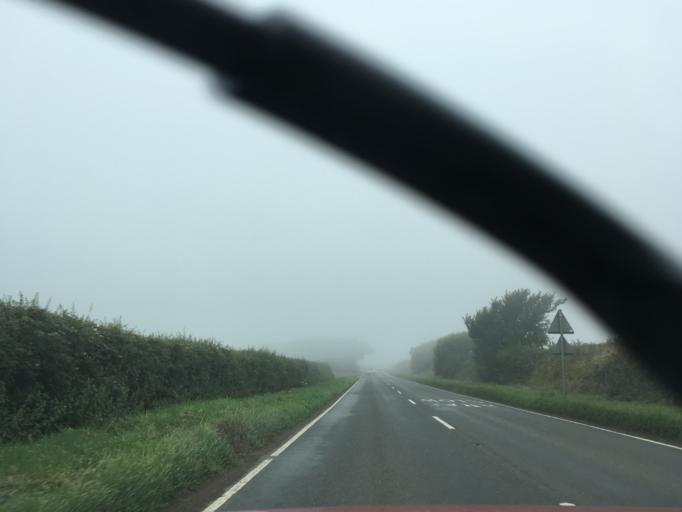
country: GB
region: Wales
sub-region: Pembrokeshire
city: Llanrhian
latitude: 51.8703
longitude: -5.1468
